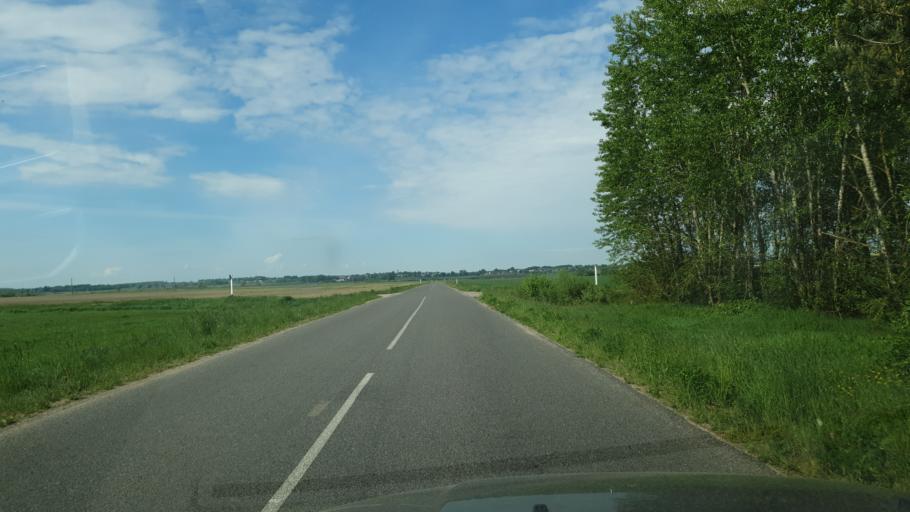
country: BY
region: Grodnenskaya
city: Mir
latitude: 53.4218
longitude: 26.3587
